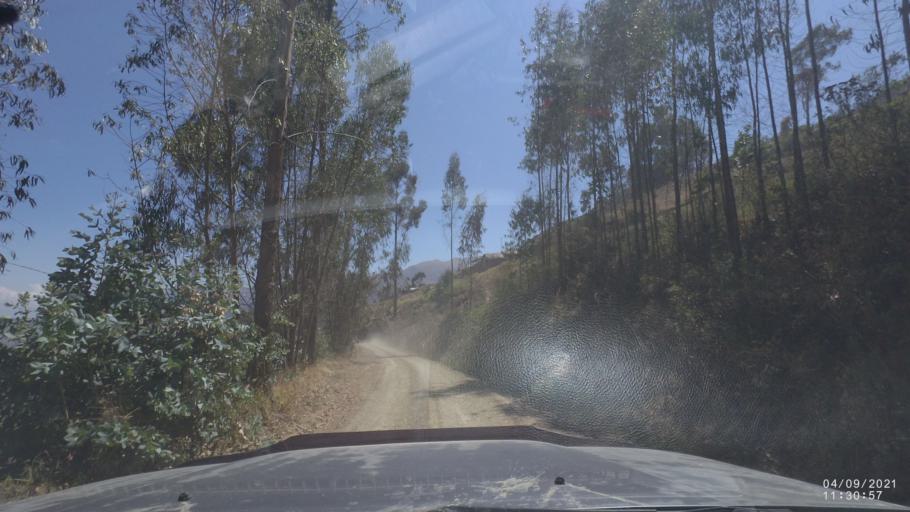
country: BO
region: Cochabamba
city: Colchani
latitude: -17.2350
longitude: -66.5207
